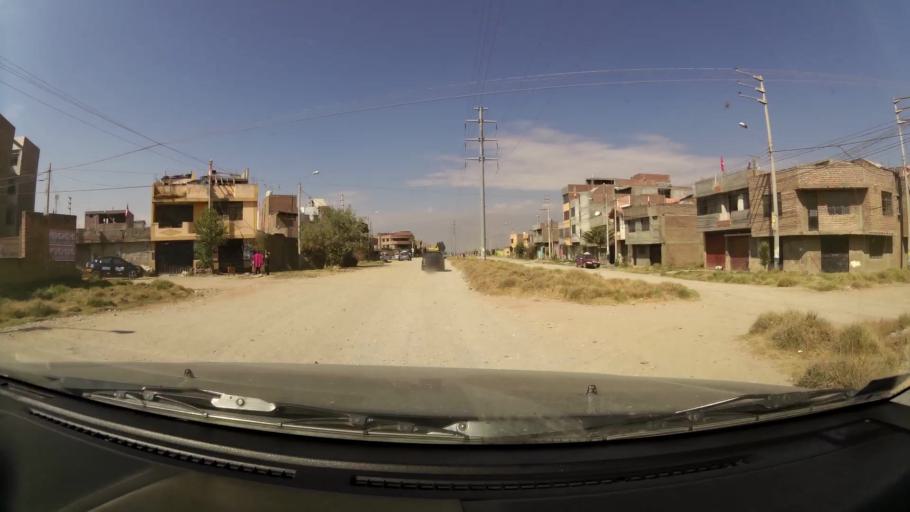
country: PE
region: Junin
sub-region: Provincia de Huancayo
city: El Tambo
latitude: -12.0733
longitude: -75.2294
